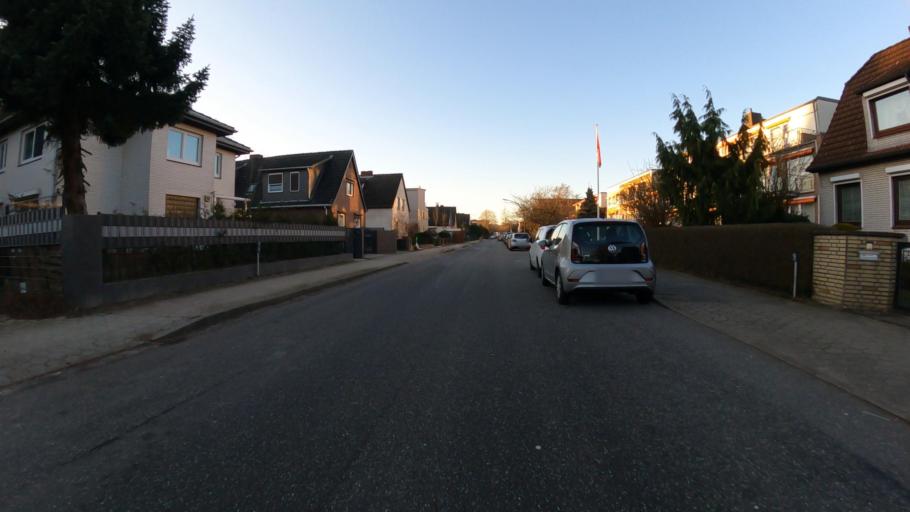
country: DE
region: Hamburg
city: Eidelstedt
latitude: 53.5995
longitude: 9.8957
